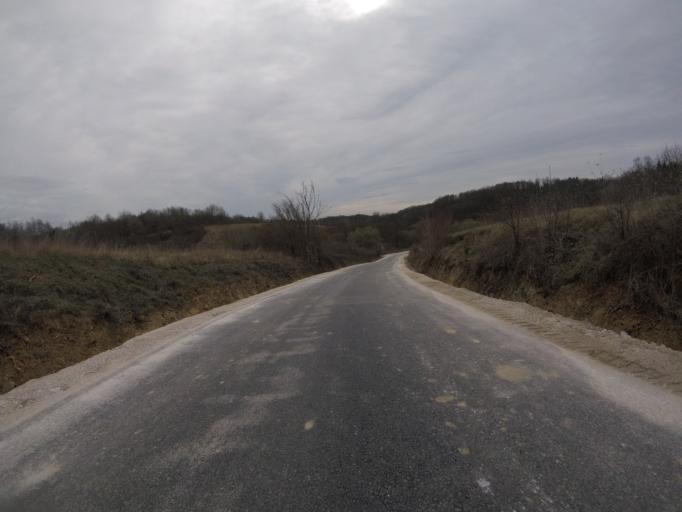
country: HR
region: Grad Zagreb
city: Strmec
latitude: 45.6052
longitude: 15.9105
